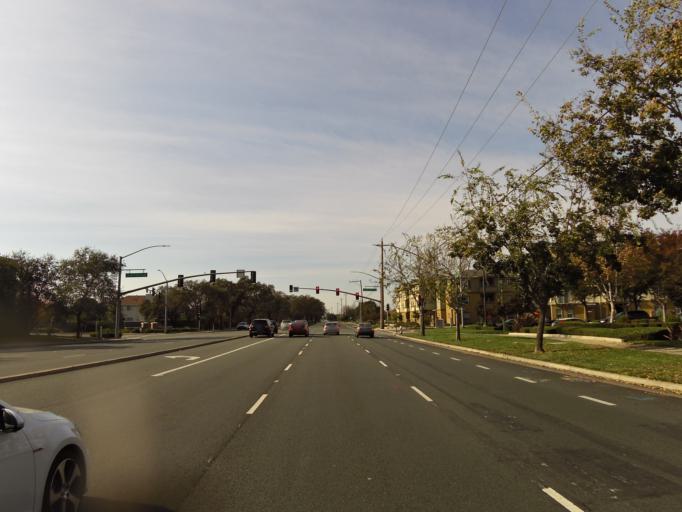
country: US
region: California
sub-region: Sacramento County
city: Laguna
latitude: 38.4090
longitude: -121.4204
